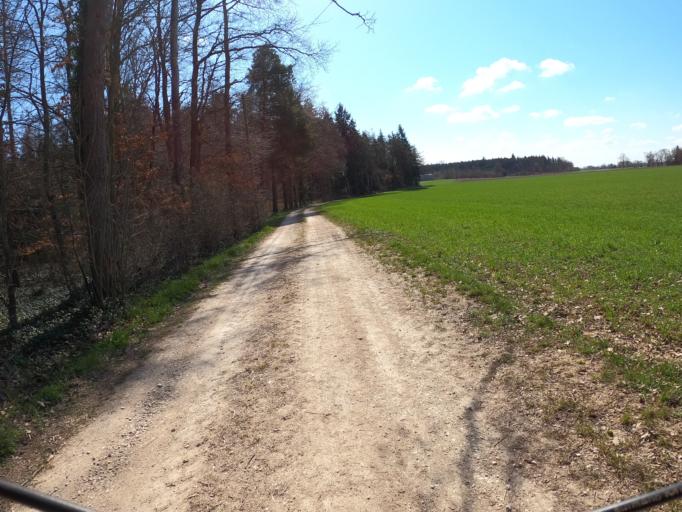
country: DE
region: Bavaria
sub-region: Swabia
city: Nersingen
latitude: 48.4038
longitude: 10.1445
